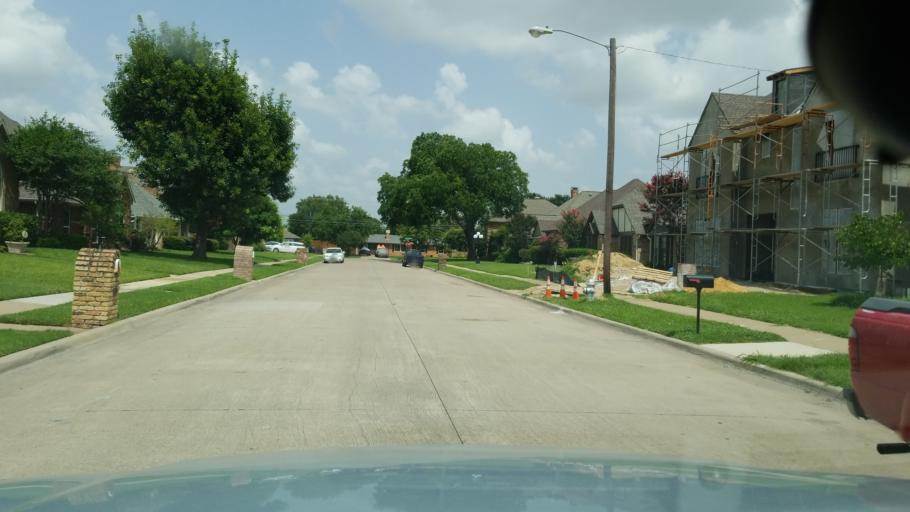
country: US
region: Texas
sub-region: Dallas County
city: Irving
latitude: 32.8191
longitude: -96.9269
